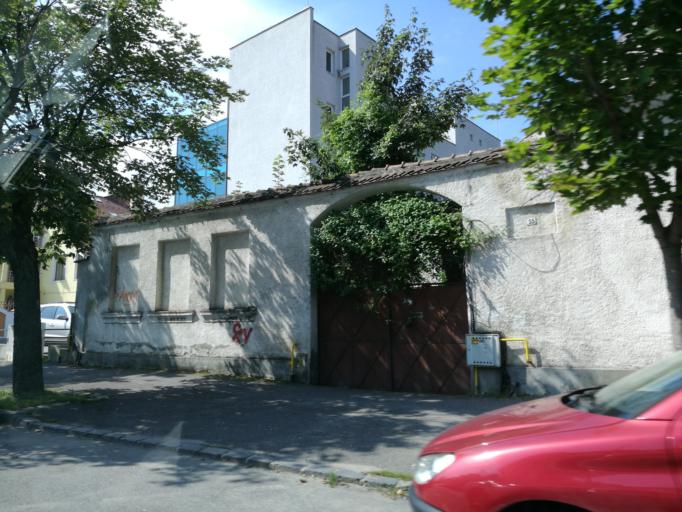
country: RO
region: Brasov
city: Brasov
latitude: 45.6560
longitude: 25.5903
